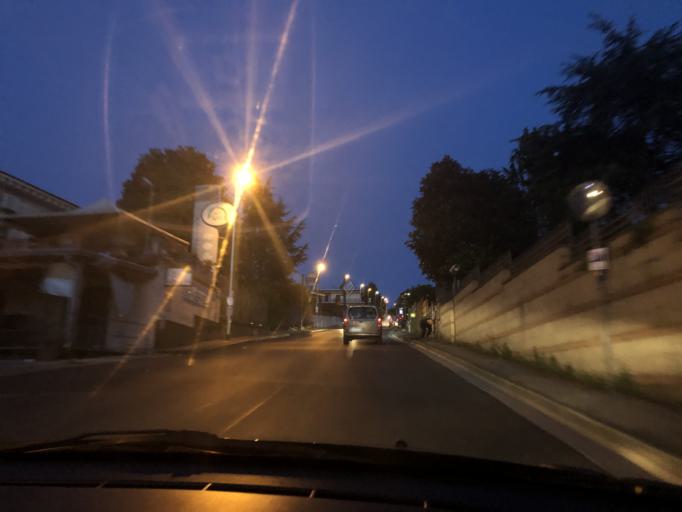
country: IT
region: Campania
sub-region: Provincia di Napoli
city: Marano di Napoli
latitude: 40.8872
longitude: 14.1804
